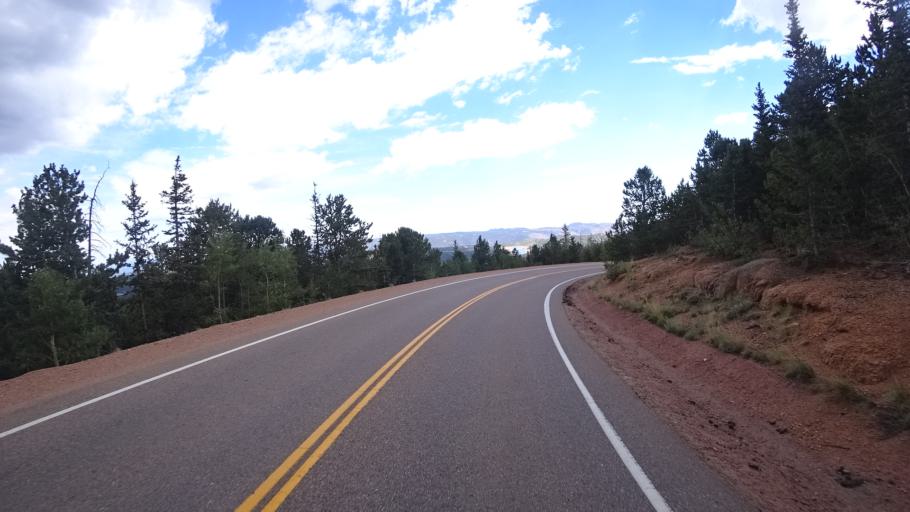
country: US
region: Colorado
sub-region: El Paso County
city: Cascade-Chipita Park
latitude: 38.8948
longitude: -105.0641
